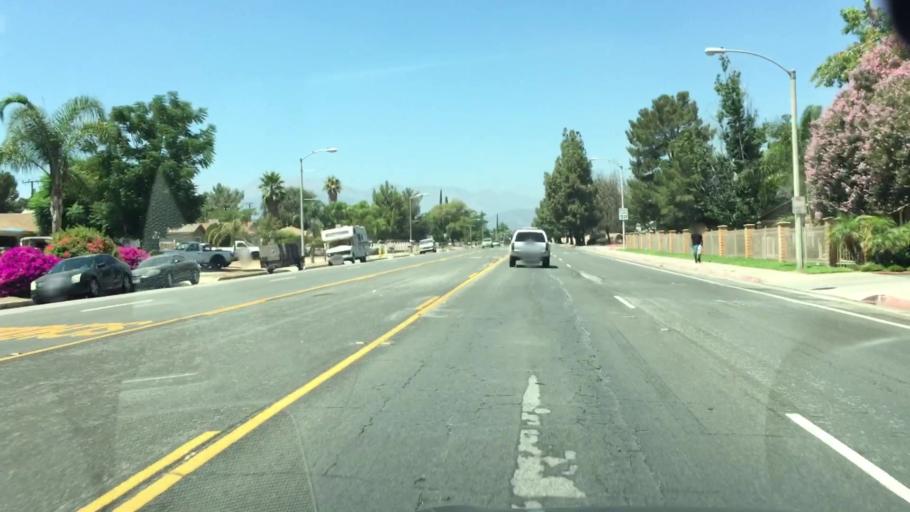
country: US
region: California
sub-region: San Bernardino County
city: Muscoy
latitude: 34.1708
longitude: -117.3194
